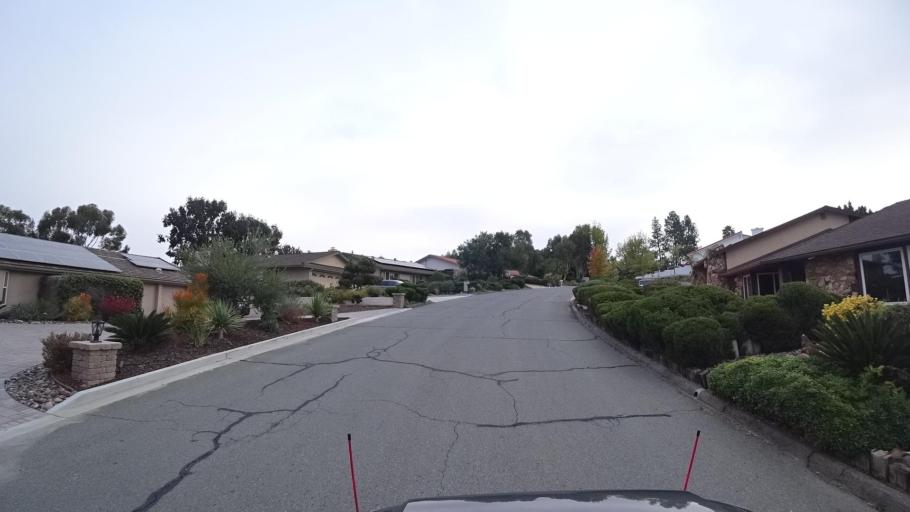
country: US
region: California
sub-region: San Diego County
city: Granite Hills
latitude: 32.7754
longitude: -116.9154
